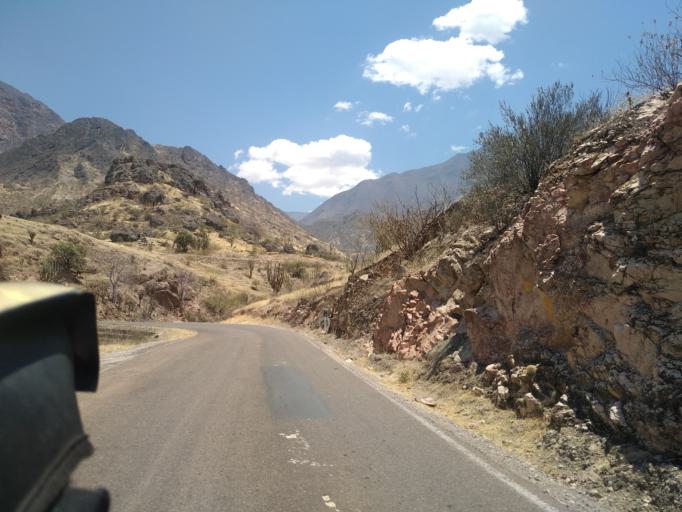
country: PE
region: Amazonas
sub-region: Provincia de Chachapoyas
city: Balsas
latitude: -6.8538
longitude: -78.0284
